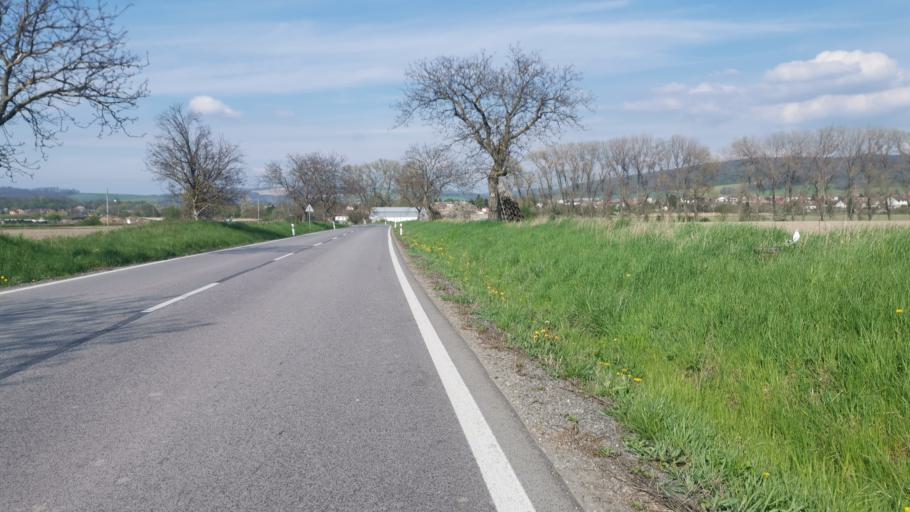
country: SK
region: Trnavsky
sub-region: Okres Senica
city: Senica
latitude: 48.5991
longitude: 17.4111
